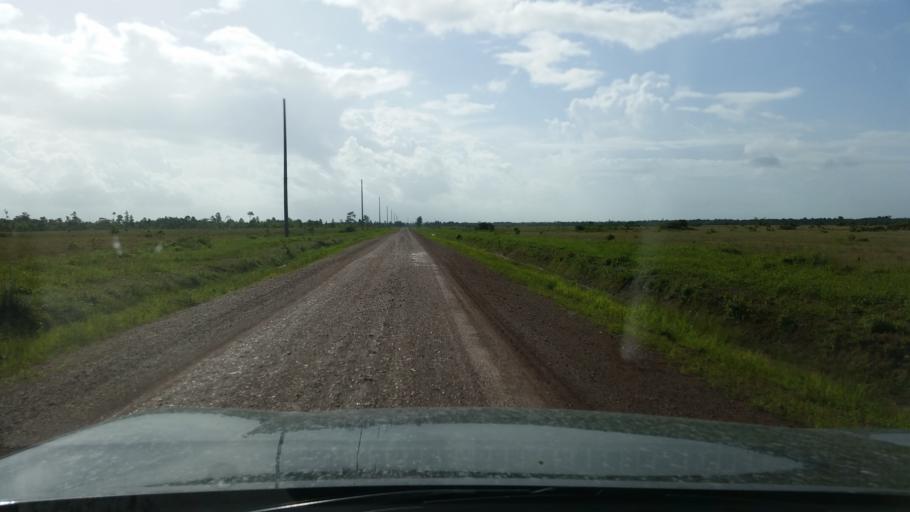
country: NI
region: Atlantico Norte (RAAN)
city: Puerto Cabezas
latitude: 14.1090
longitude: -83.5811
